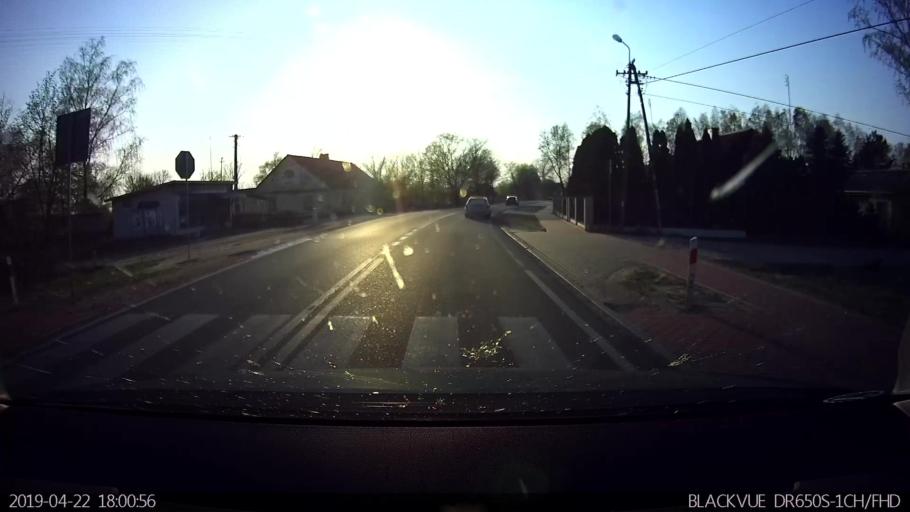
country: PL
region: Masovian Voivodeship
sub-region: Powiat wegrowski
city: Korytnica
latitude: 52.4768
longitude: 21.8385
